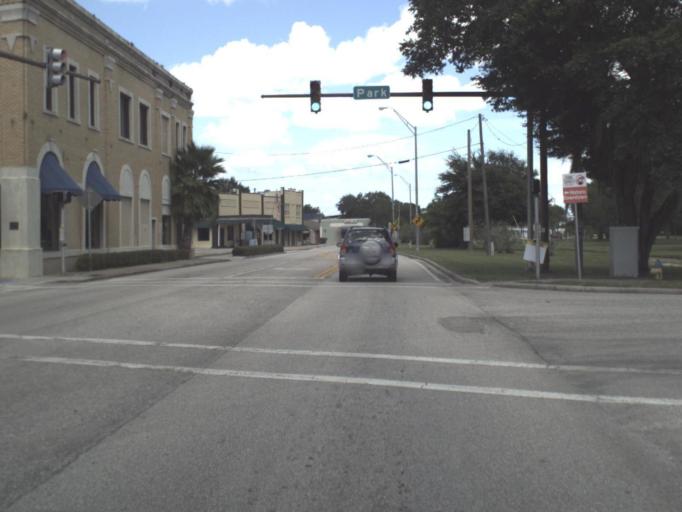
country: US
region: Florida
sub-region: Polk County
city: Lake Wales
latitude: 27.9025
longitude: -81.5868
